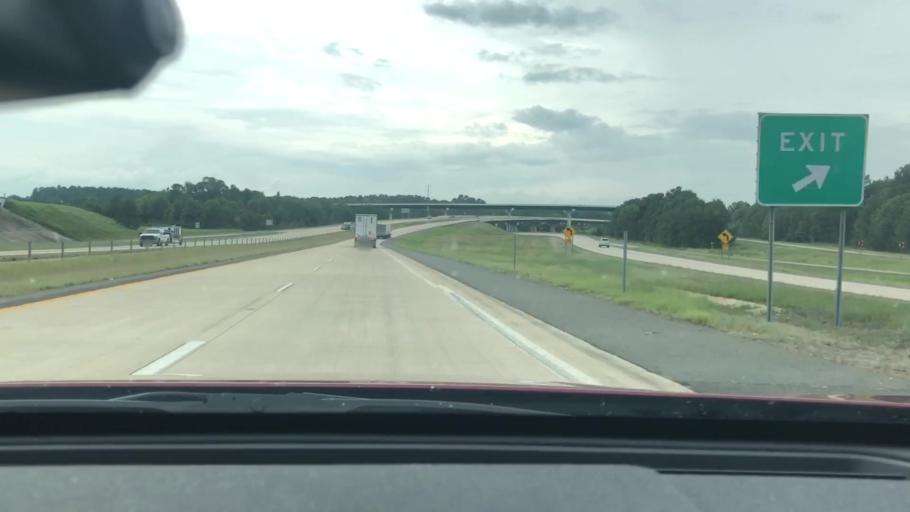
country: US
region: Texas
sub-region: Bowie County
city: Texarkana
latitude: 33.3908
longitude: -94.0161
